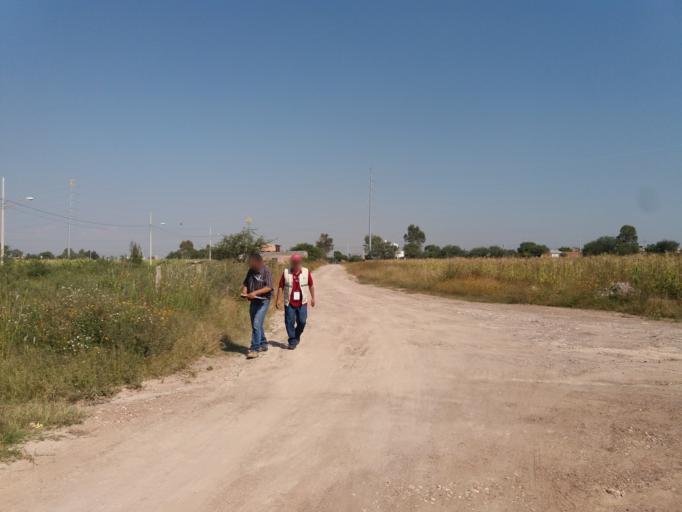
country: MX
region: Aguascalientes
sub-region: Aguascalientes
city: Penuelas (El Cienegal)
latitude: 21.7494
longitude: -102.2599
